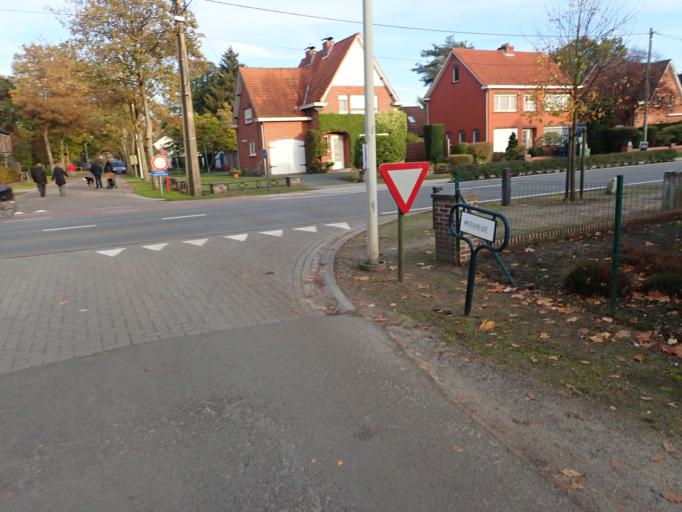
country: BE
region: Flanders
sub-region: Provincie Antwerpen
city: Zoersel
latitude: 51.2777
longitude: 4.7085
